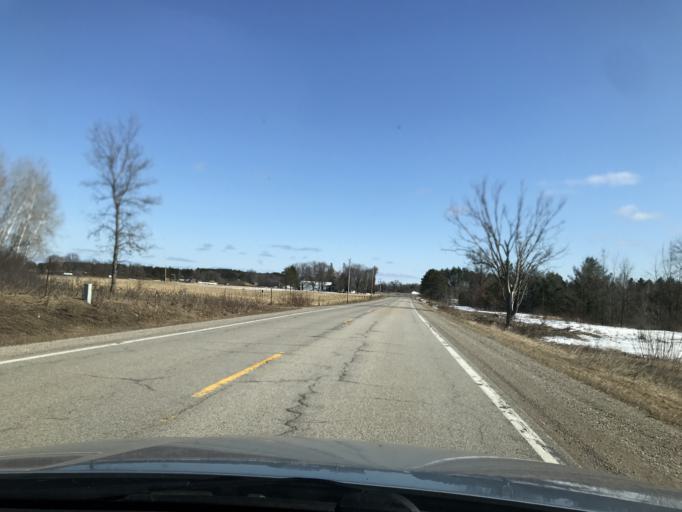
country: US
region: Wisconsin
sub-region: Marinette County
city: Peshtigo
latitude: 45.2457
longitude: -88.0332
